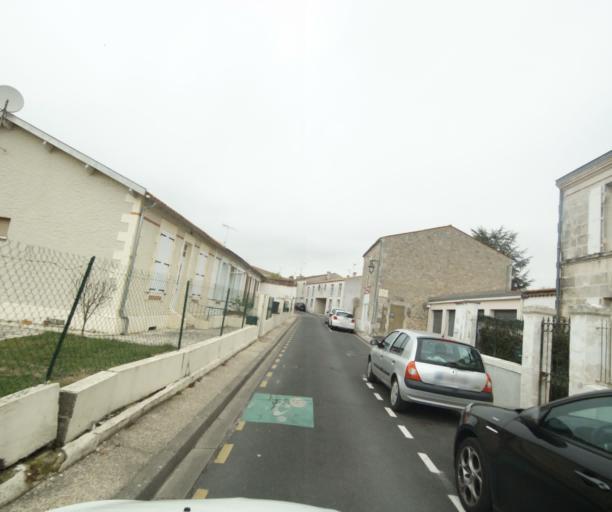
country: FR
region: Poitou-Charentes
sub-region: Departement de la Charente-Maritime
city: Saintes
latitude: 45.7441
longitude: -0.6215
